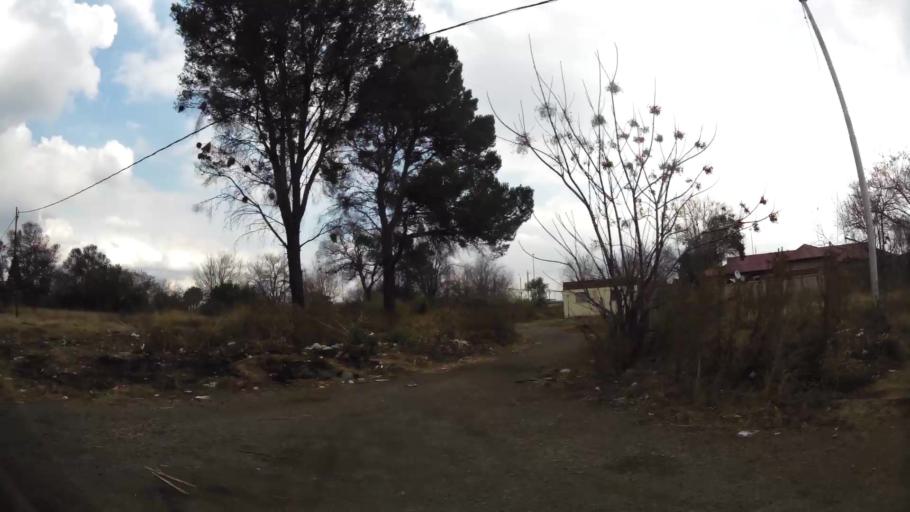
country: ZA
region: Gauteng
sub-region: Sedibeng District Municipality
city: Vereeniging
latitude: -26.6763
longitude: 27.9365
